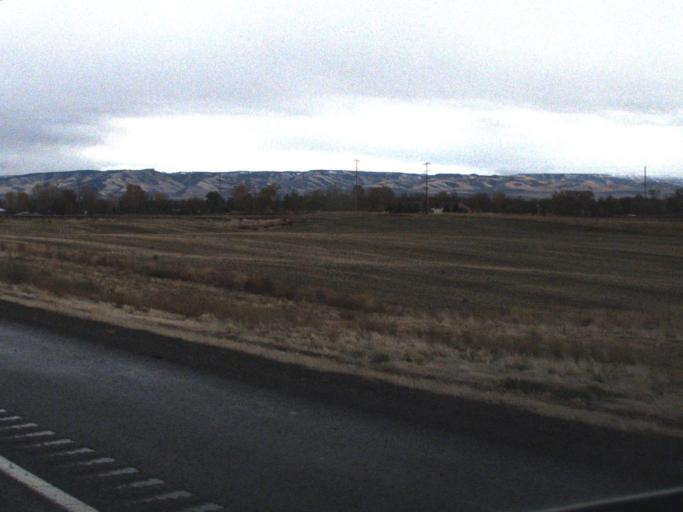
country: US
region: Washington
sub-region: Walla Walla County
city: Garrett
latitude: 46.0548
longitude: -118.4600
